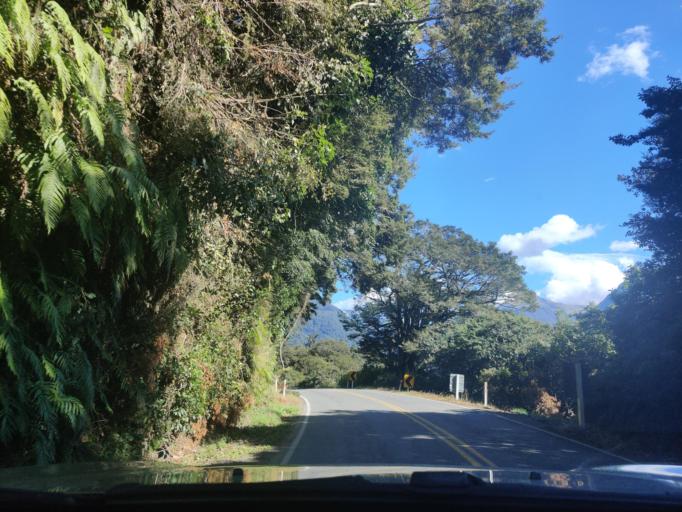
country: NZ
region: Otago
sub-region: Queenstown-Lakes District
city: Wanaka
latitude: -43.9707
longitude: 169.4099
